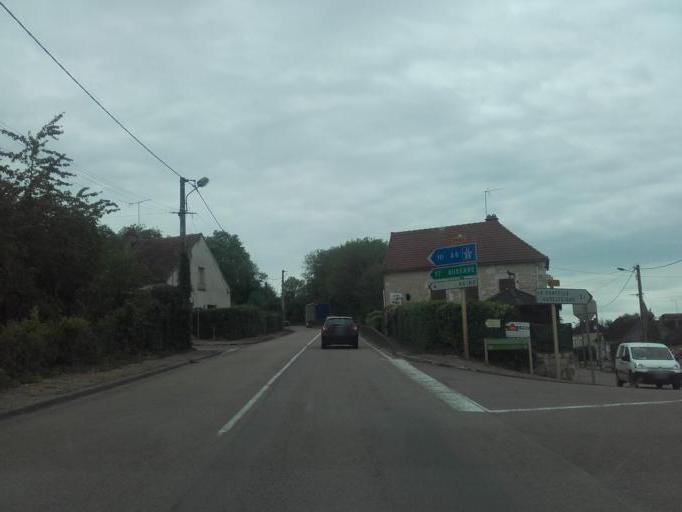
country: FR
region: Bourgogne
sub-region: Departement de l'Yonne
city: Chablis
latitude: 47.8222
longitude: 3.7745
